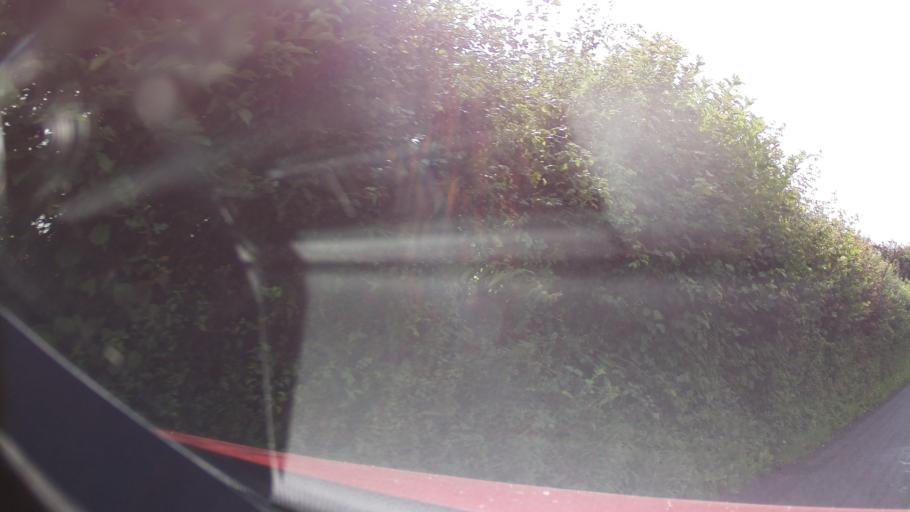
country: GB
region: England
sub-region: Somerset
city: Evercreech
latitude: 51.1616
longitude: -2.5041
